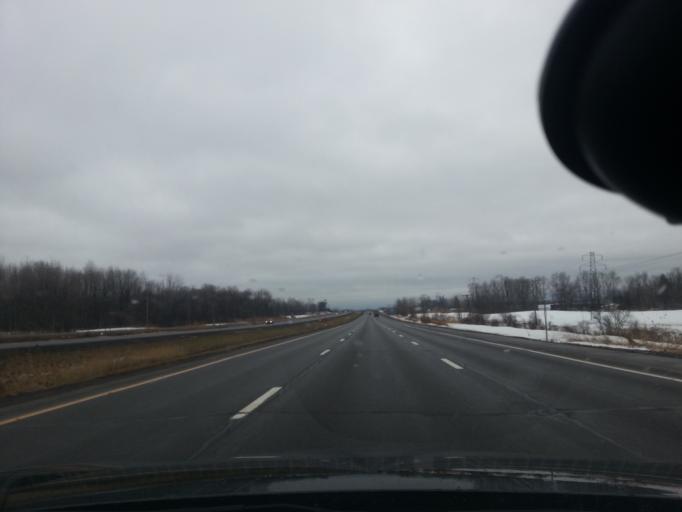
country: US
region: New York
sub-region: Onondaga County
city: Brewerton
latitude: 43.1906
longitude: -76.1217
